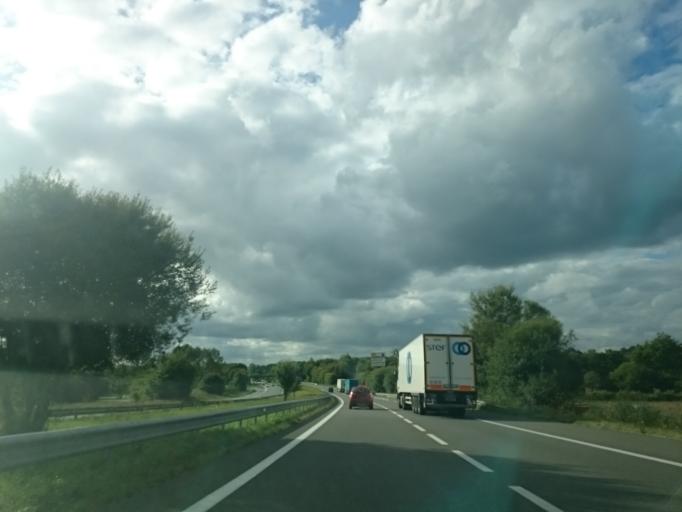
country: FR
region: Brittany
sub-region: Departement d'Ille-et-Vilaine
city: Montauban-de-Bretagne
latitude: 48.2066
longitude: -2.0402
